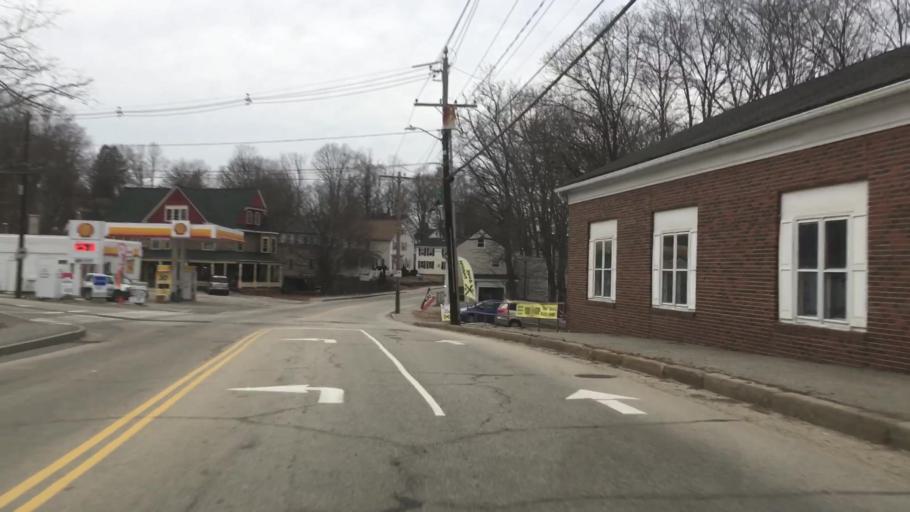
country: US
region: New Hampshire
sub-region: Hillsborough County
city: Milford
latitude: 42.8334
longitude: -71.6441
